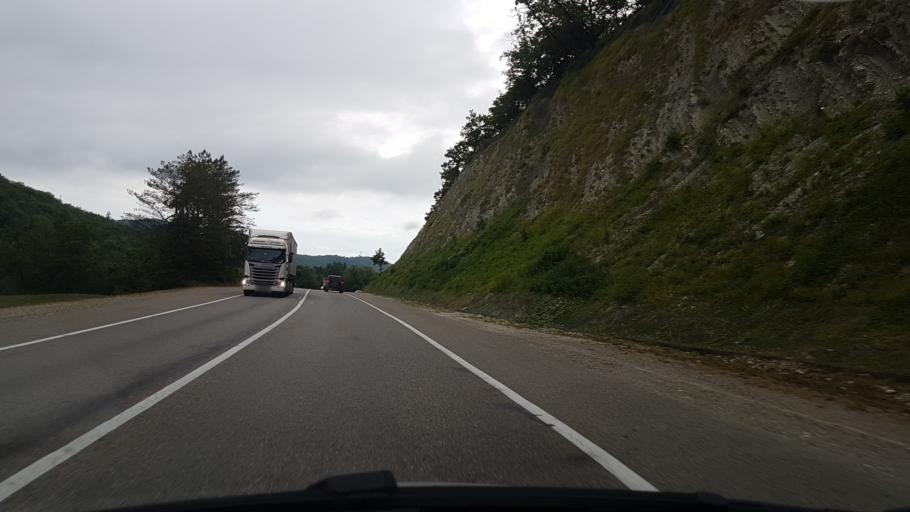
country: RU
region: Krasnodarskiy
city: Ol'ginka
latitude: 44.2314
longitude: 38.8965
